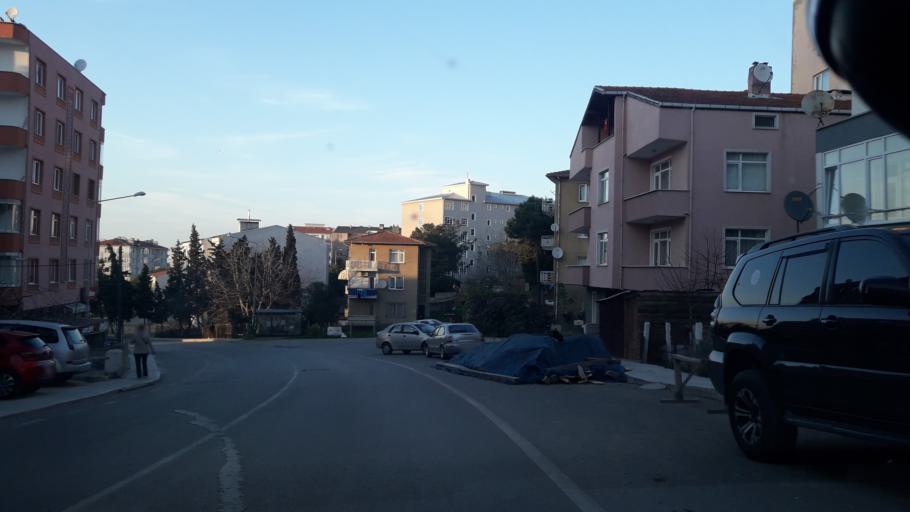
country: TR
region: Sinop
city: Sinop
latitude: 42.0267
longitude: 35.1609
